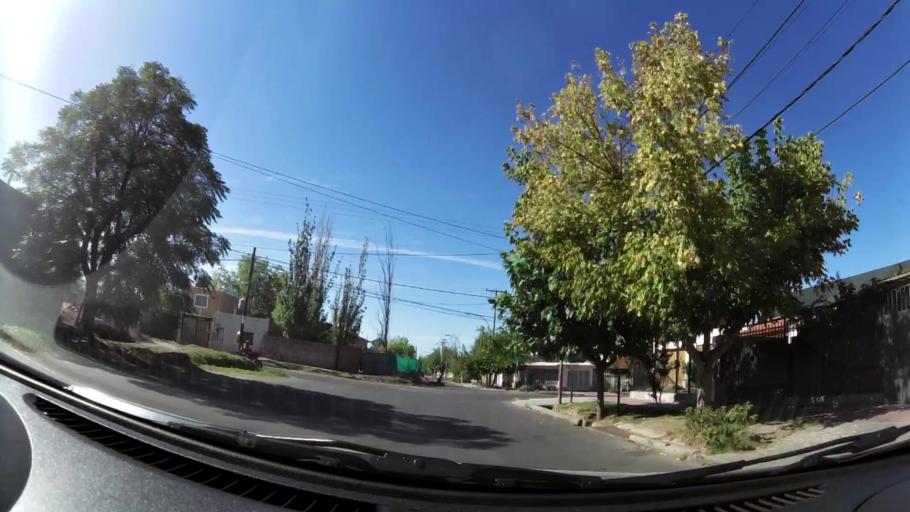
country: AR
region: Mendoza
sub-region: Departamento de Godoy Cruz
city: Godoy Cruz
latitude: -32.9419
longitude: -68.8094
